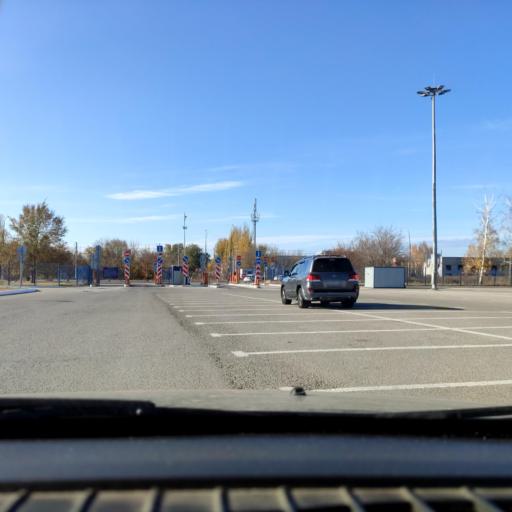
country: RU
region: Samara
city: Tol'yatti
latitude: 53.5446
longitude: 49.3032
